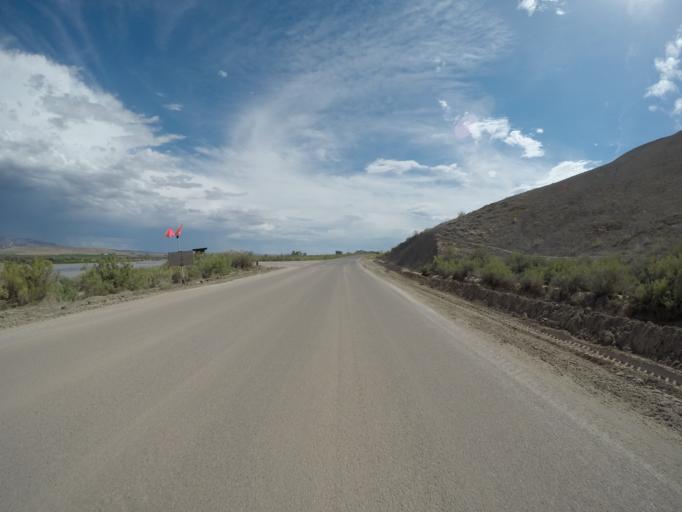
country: US
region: Utah
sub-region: Uintah County
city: Naples
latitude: 40.4328
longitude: -109.3312
